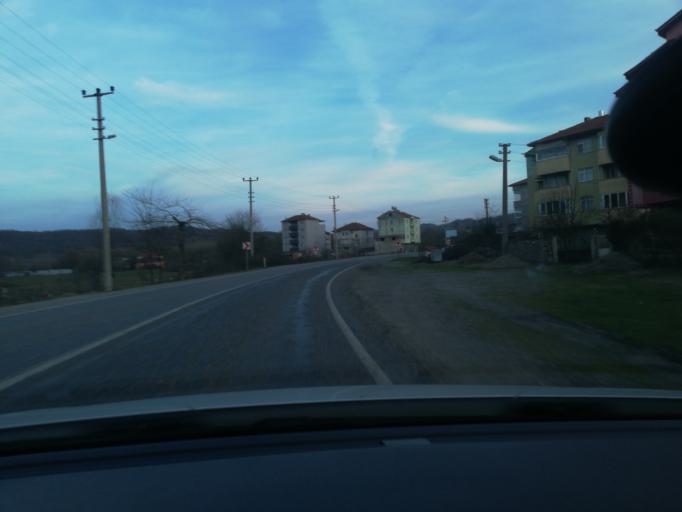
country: TR
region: Zonguldak
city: Saltukova
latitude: 41.5265
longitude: 32.1000
